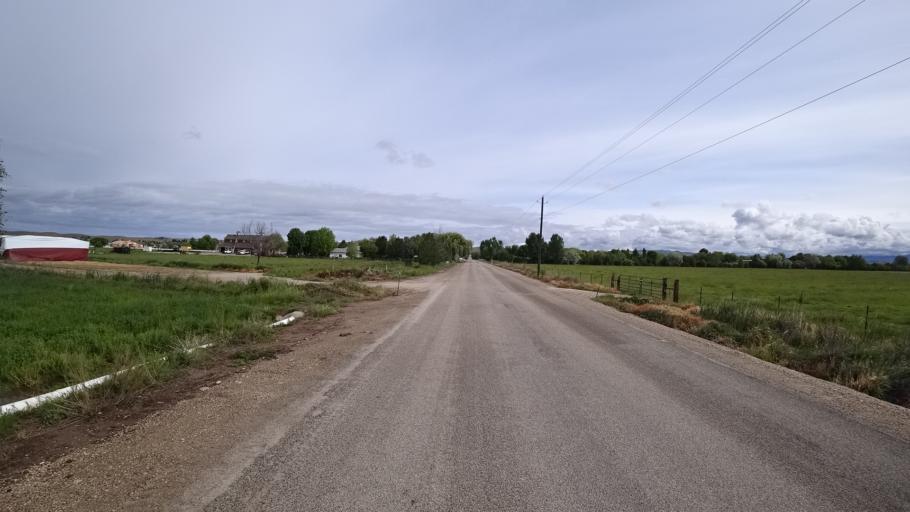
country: US
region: Idaho
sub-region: Ada County
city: Eagle
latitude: 43.7230
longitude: -116.4035
